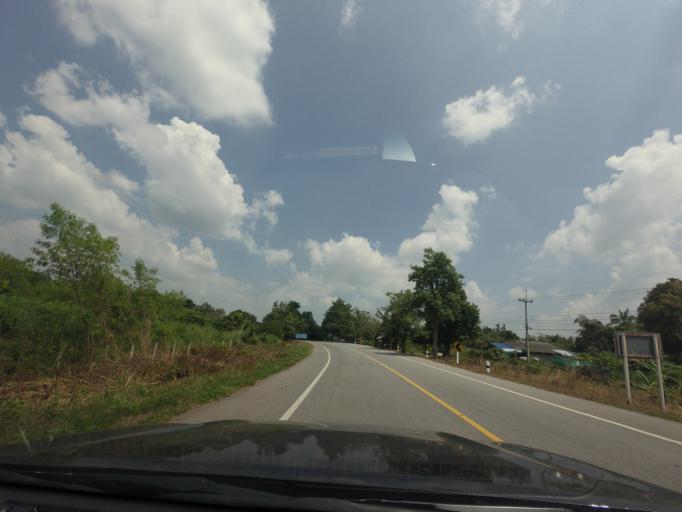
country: TH
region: Phitsanulok
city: Chat Trakan
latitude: 17.2996
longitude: 100.4241
